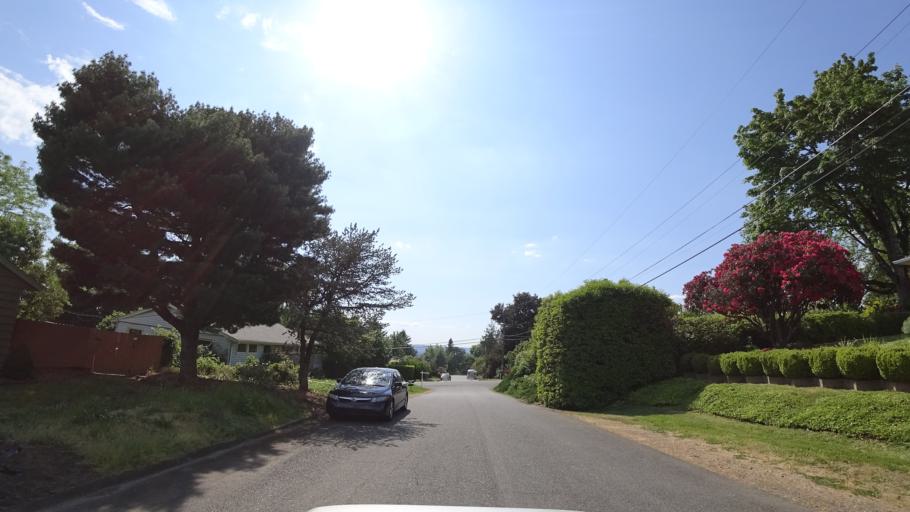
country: US
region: Oregon
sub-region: Washington County
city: Metzger
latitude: 45.4513
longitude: -122.7402
